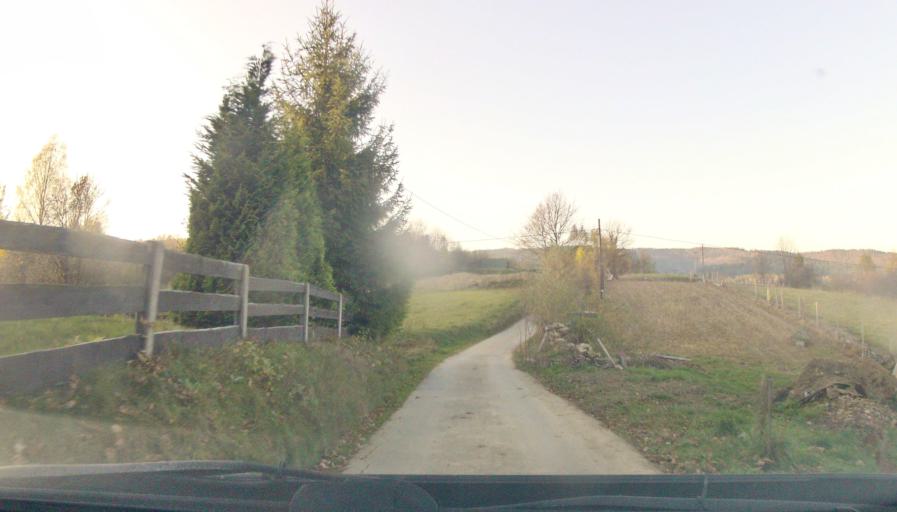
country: PL
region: Silesian Voivodeship
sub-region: Powiat zywiecki
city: Slemien
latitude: 49.7358
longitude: 19.4176
